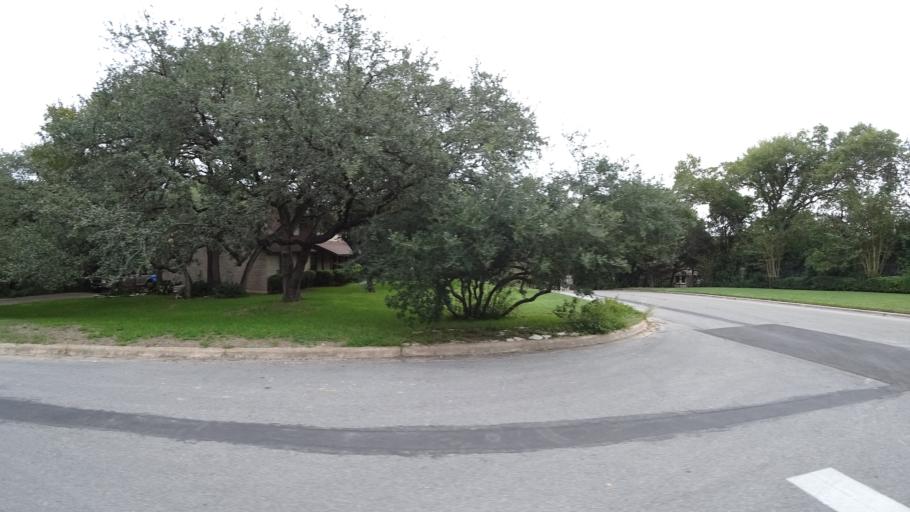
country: US
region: Texas
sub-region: Travis County
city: Rollingwood
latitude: 30.2792
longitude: -97.7864
